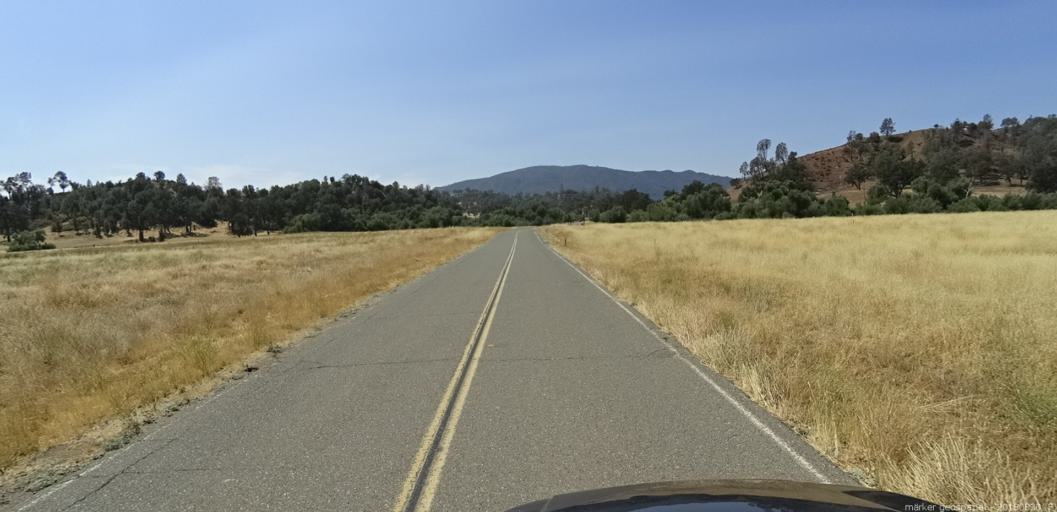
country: US
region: California
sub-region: Monterey County
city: King City
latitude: 35.9657
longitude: -121.2739
